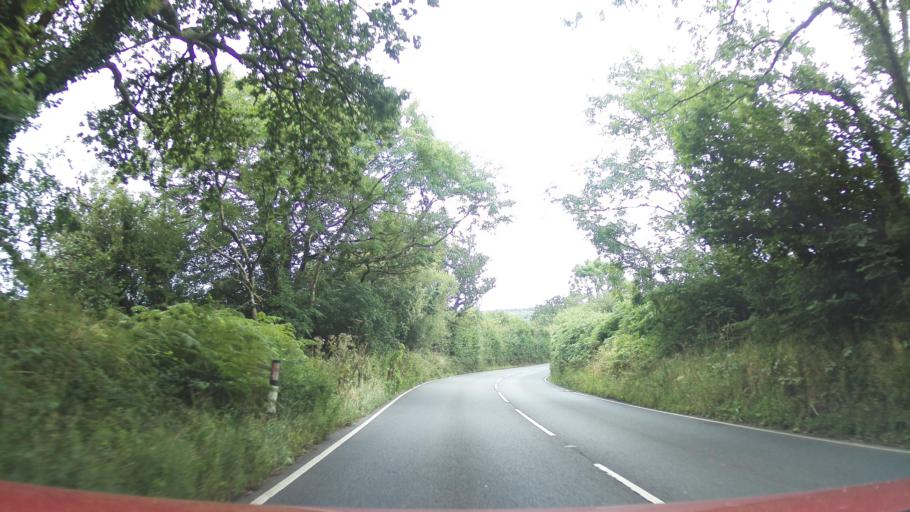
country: GB
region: England
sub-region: Devon
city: Bishopsteignton
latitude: 50.5945
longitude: -3.5410
